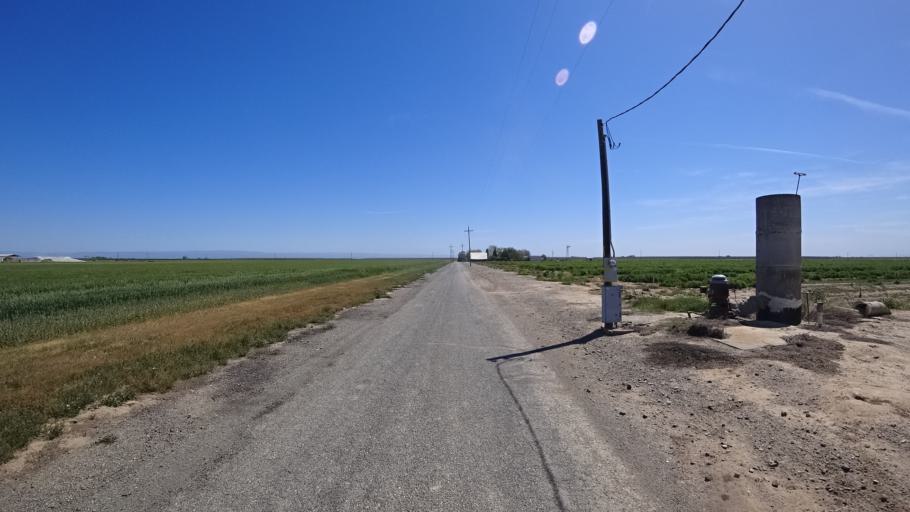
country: US
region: California
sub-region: Glenn County
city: Orland
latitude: 39.6383
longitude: -122.1276
